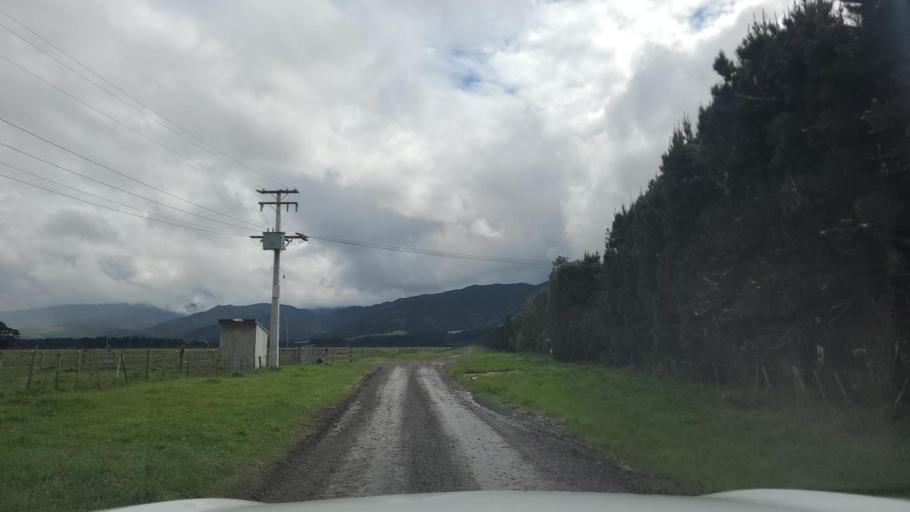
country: NZ
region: Wellington
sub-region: Upper Hutt City
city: Upper Hutt
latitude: -41.1318
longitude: 175.3229
